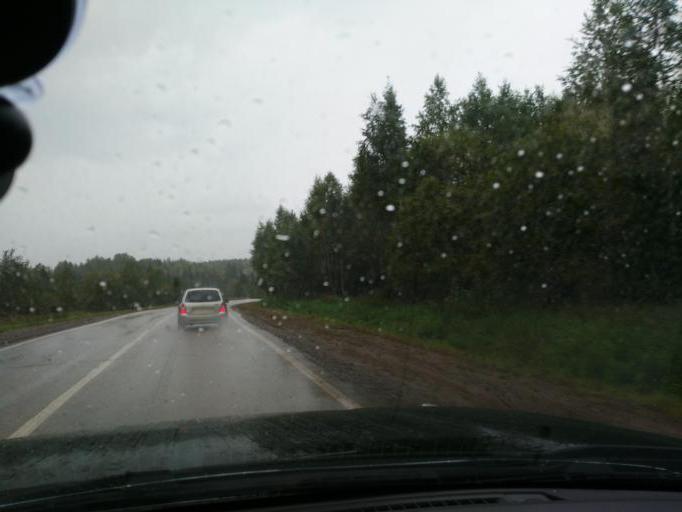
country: RU
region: Perm
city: Barda
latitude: 56.9091
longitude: 55.6816
